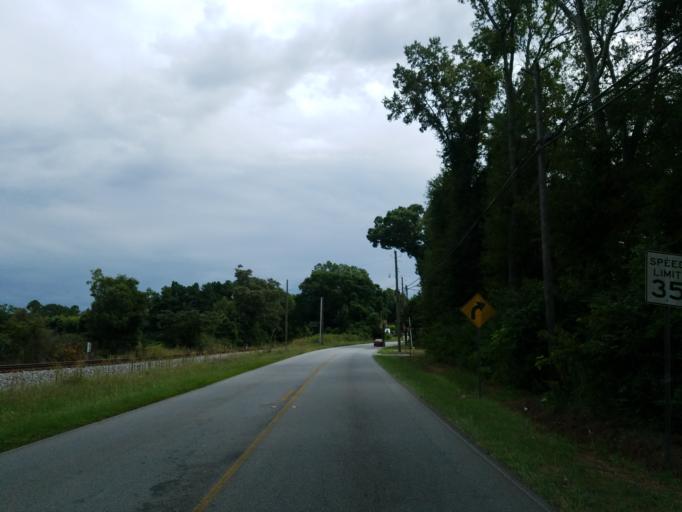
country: US
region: Georgia
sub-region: Spalding County
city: Experiment
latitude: 33.2800
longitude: -84.2830
